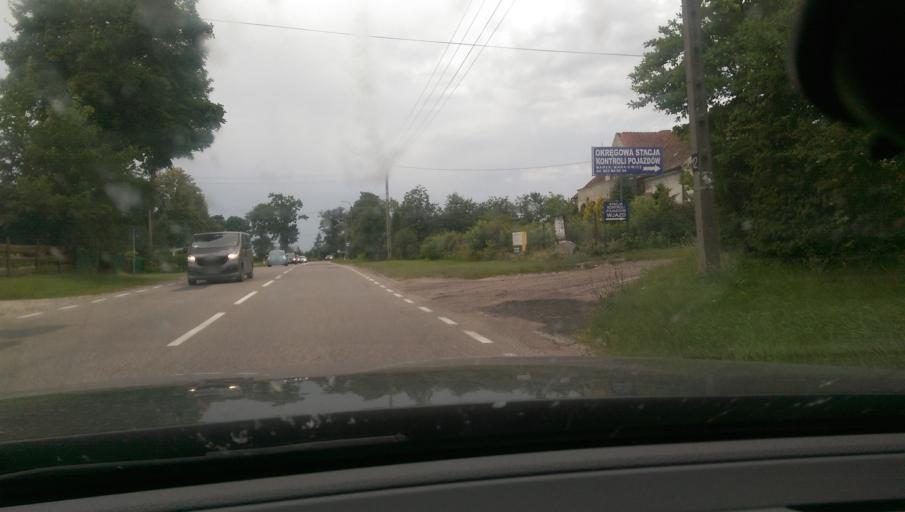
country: PL
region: Podlasie
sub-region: Powiat grajewski
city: Rajgrod
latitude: 53.8677
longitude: 22.6564
